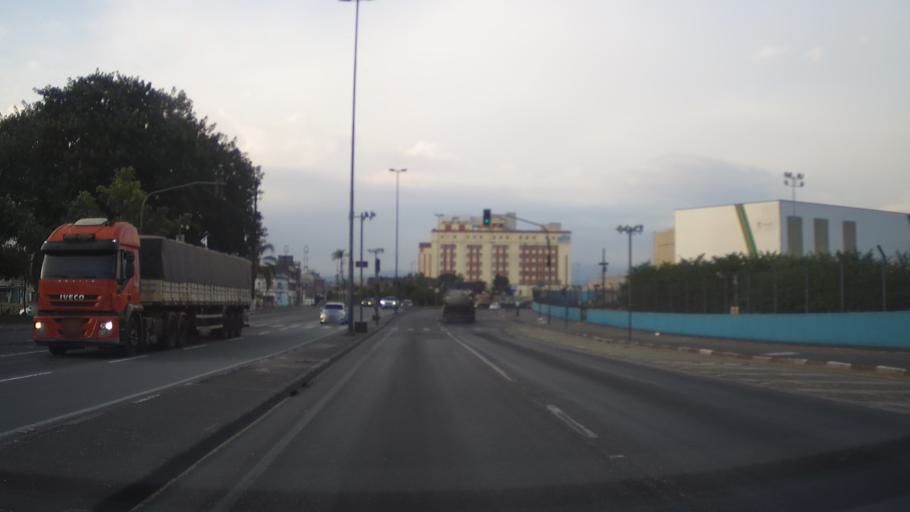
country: BR
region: Sao Paulo
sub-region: Santos
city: Santos
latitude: -23.9418
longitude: -46.3172
